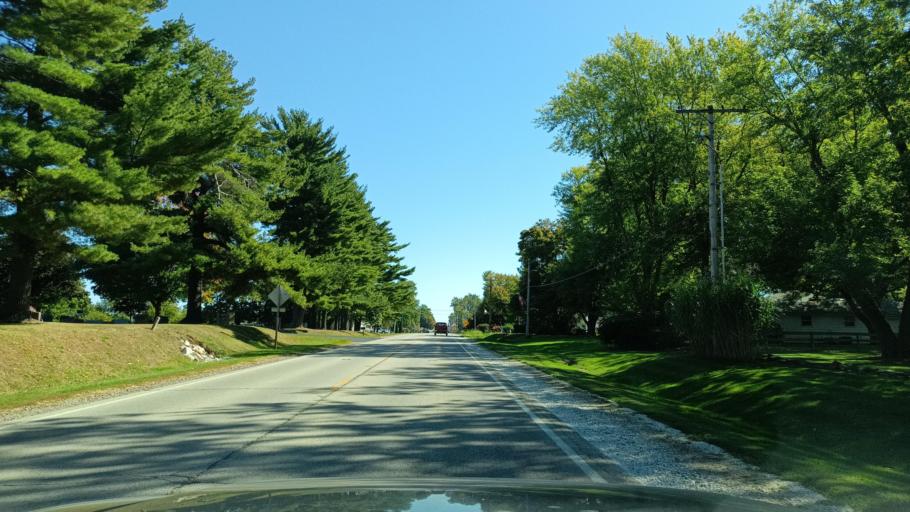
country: US
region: Illinois
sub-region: Peoria County
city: Dunlap
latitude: 40.7899
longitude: -89.7560
